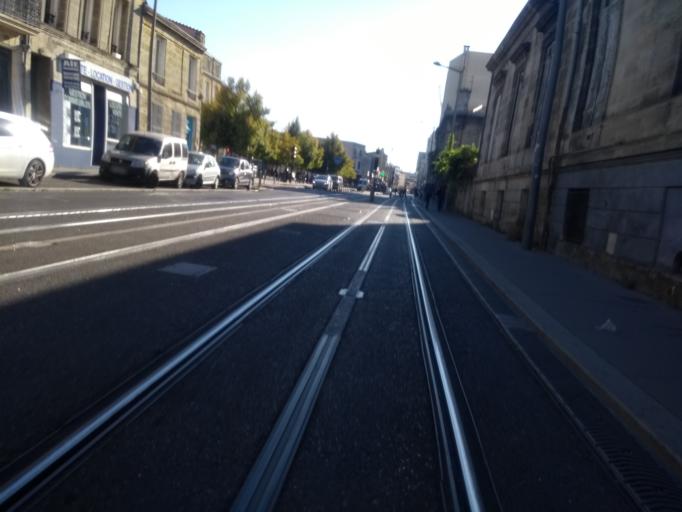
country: FR
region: Aquitaine
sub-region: Departement de la Gironde
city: Bordeaux
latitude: 44.8259
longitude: -0.5774
